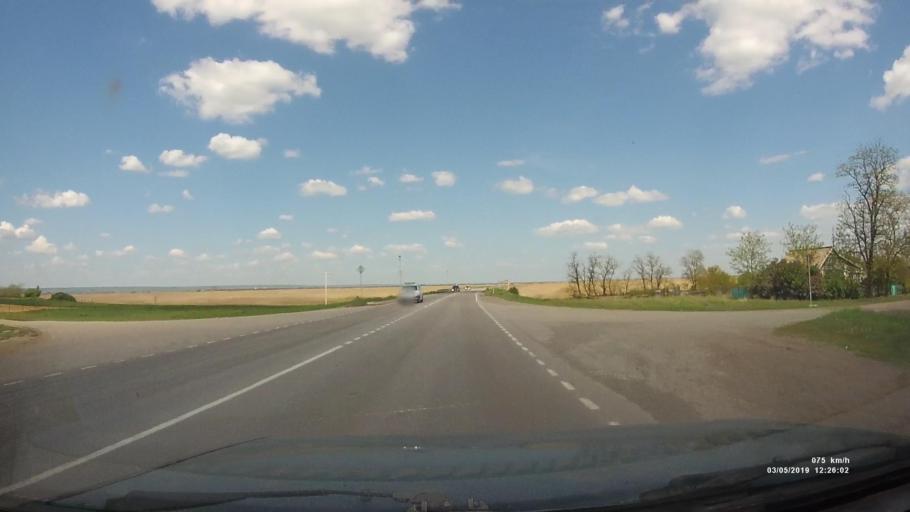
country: RU
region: Rostov
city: Semikarakorsk
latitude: 47.4400
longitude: 40.7120
